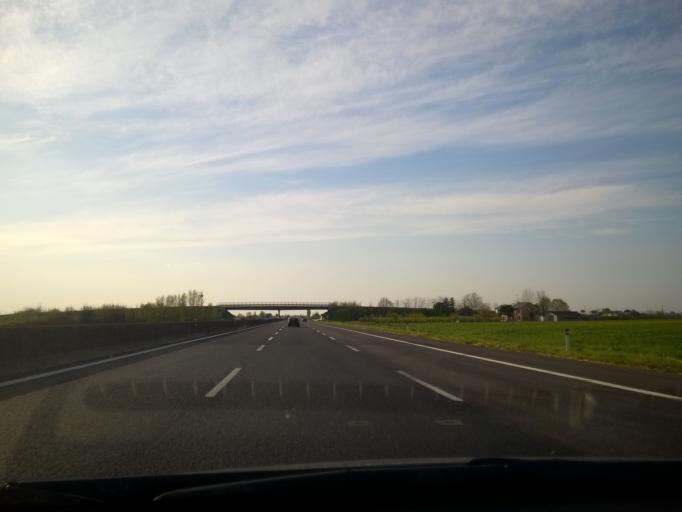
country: IT
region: Emilia-Romagna
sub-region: Forli-Cesena
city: Forlimpopoli
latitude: 44.2326
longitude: 12.1414
